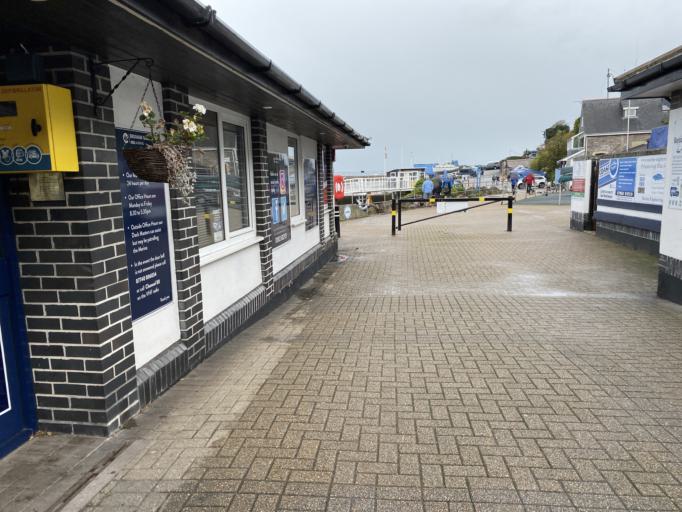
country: GB
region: England
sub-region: Borough of Torbay
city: Brixham
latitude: 50.3990
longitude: -3.5064
